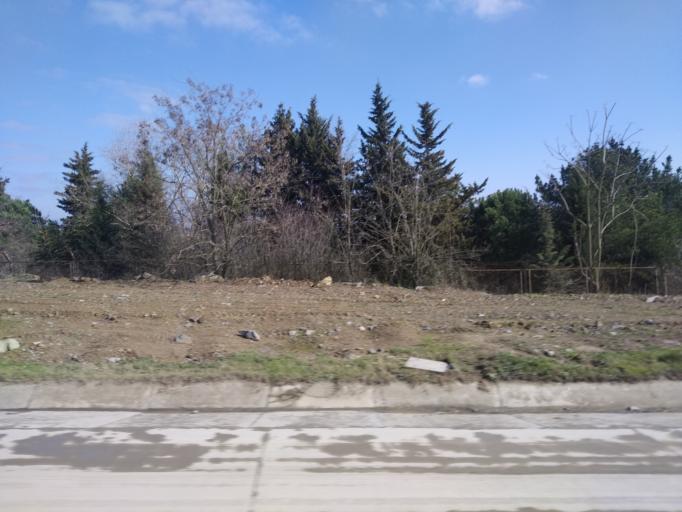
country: TR
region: Istanbul
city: Kemerburgaz
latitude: 41.1244
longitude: 28.9457
